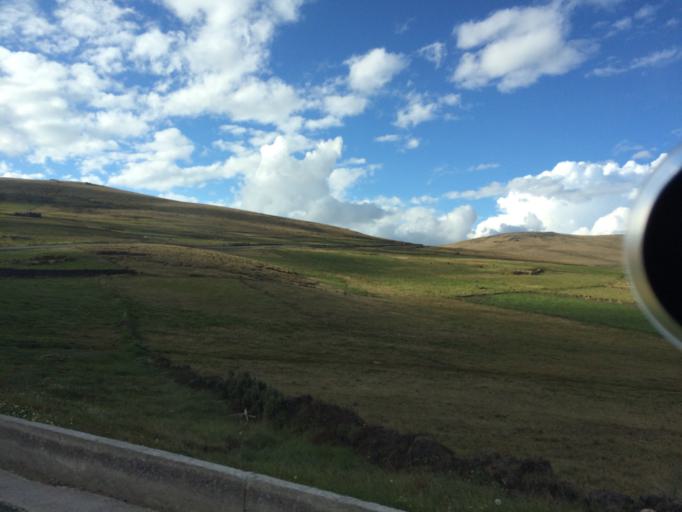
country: EC
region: Chimborazo
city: Alausi
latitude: -2.2413
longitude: -78.6804
